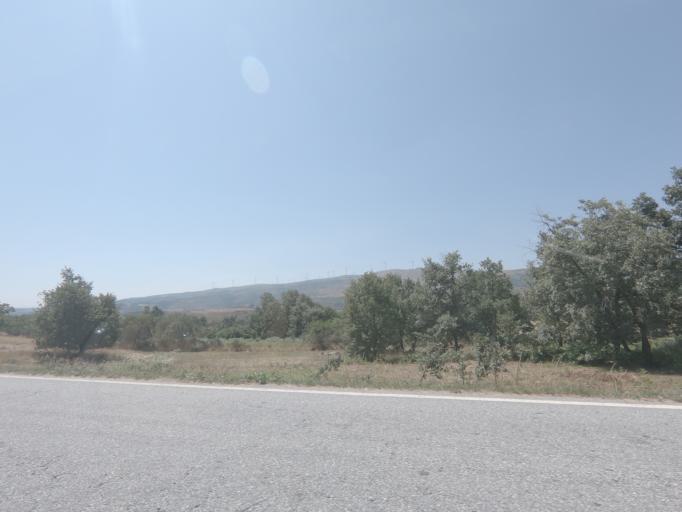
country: PT
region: Viseu
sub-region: Castro Daire
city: Castro Daire
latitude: 40.9616
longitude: -7.8862
